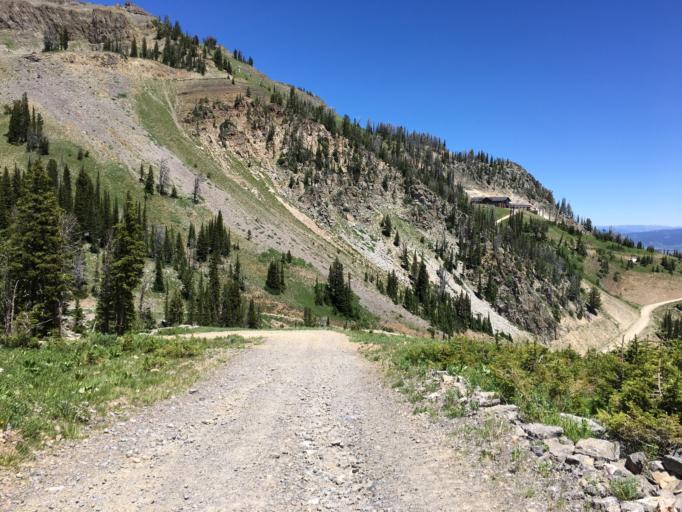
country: US
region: Wyoming
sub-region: Teton County
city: Moose Wilson Road
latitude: 43.5972
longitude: -110.8600
